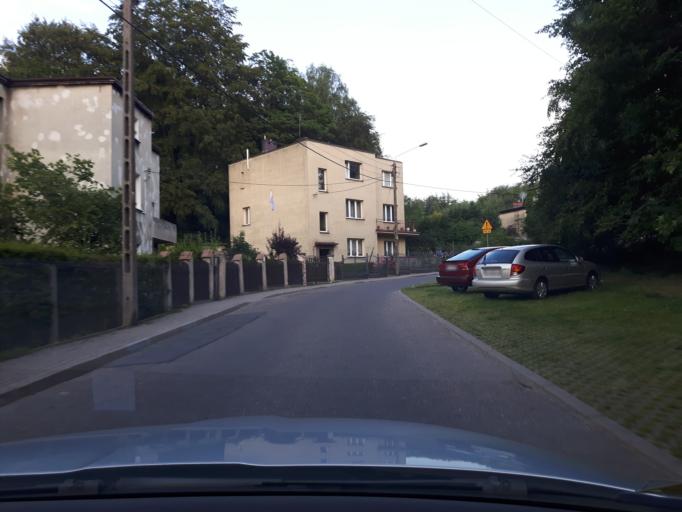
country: PL
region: Pomeranian Voivodeship
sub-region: Gdynia
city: Gdynia
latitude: 54.5136
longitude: 18.5248
